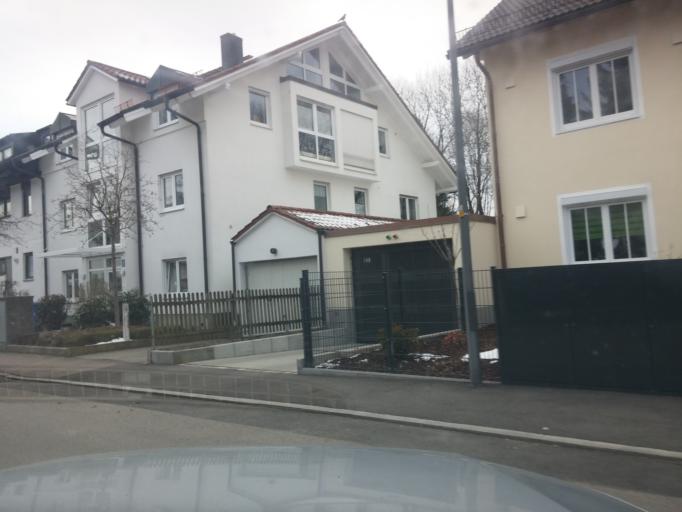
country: DE
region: Bavaria
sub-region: Upper Bavaria
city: Neubiberg
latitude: 48.1232
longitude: 11.6735
